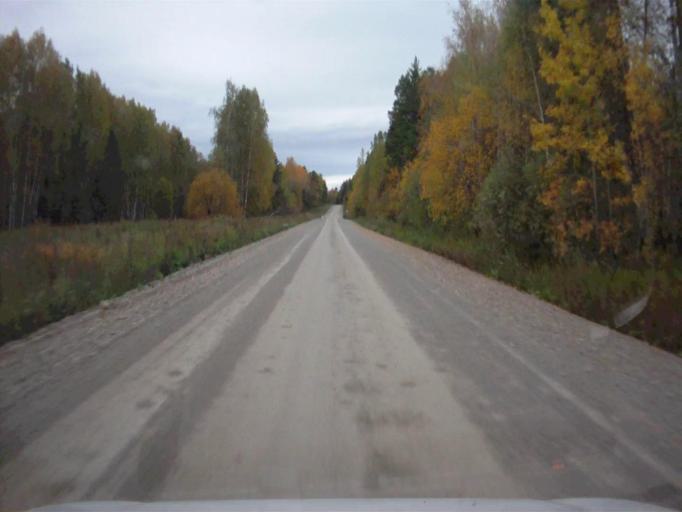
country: RU
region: Chelyabinsk
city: Nyazepetrovsk
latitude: 56.0803
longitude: 59.4231
